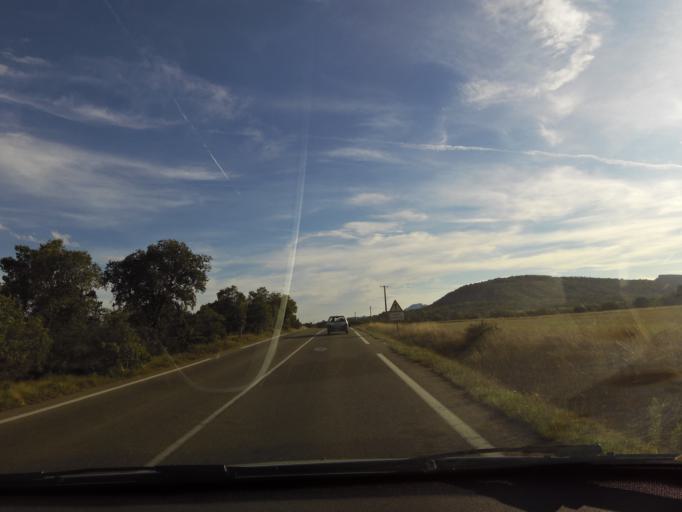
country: FR
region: Languedoc-Roussillon
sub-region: Departement de l'Herault
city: Claret
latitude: 43.8518
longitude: 3.9267
